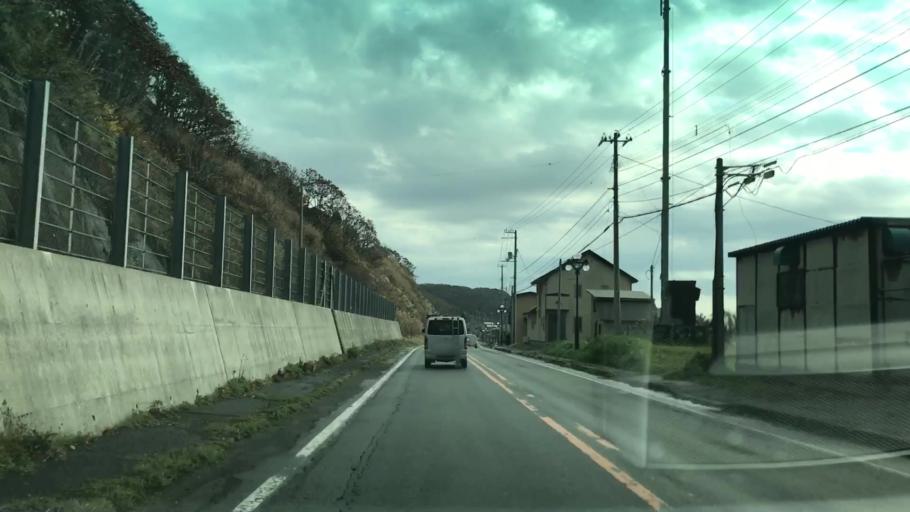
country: JP
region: Hokkaido
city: Shizunai-furukawacho
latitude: 42.1532
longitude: 142.7959
